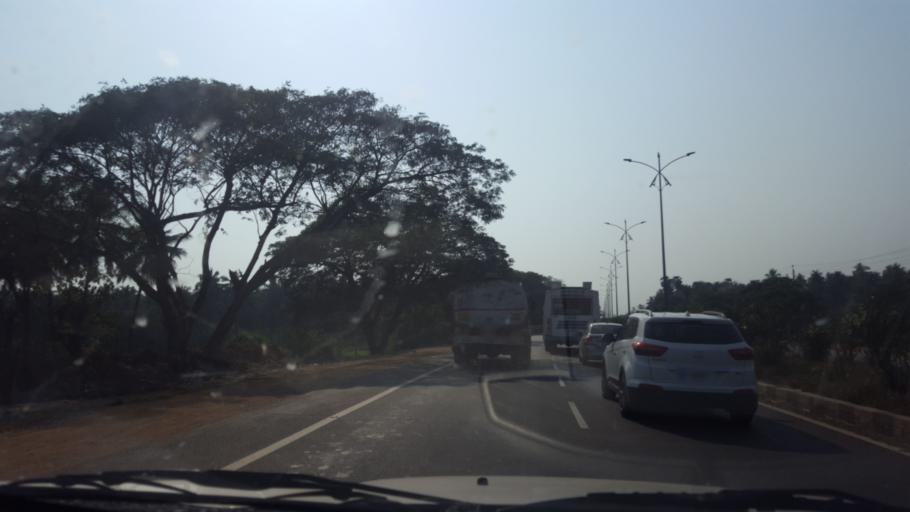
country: IN
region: Andhra Pradesh
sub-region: Vishakhapatnam
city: Anakapalle
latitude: 17.6769
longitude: 83.0226
